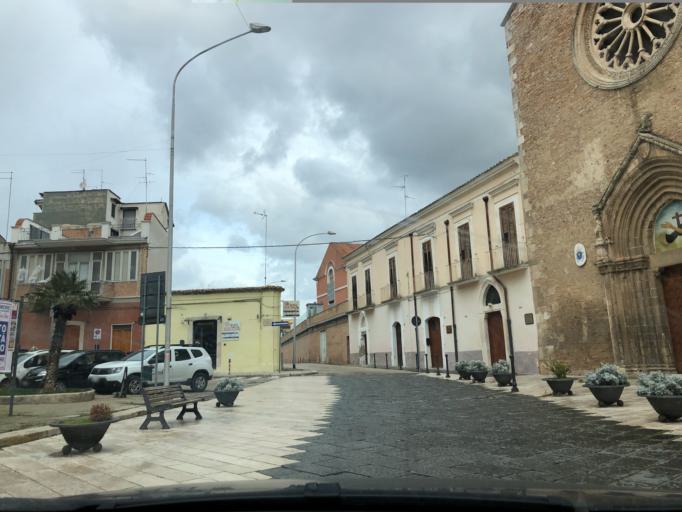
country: IT
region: Apulia
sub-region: Provincia di Foggia
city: Lucera
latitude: 41.5104
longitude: 15.3333
